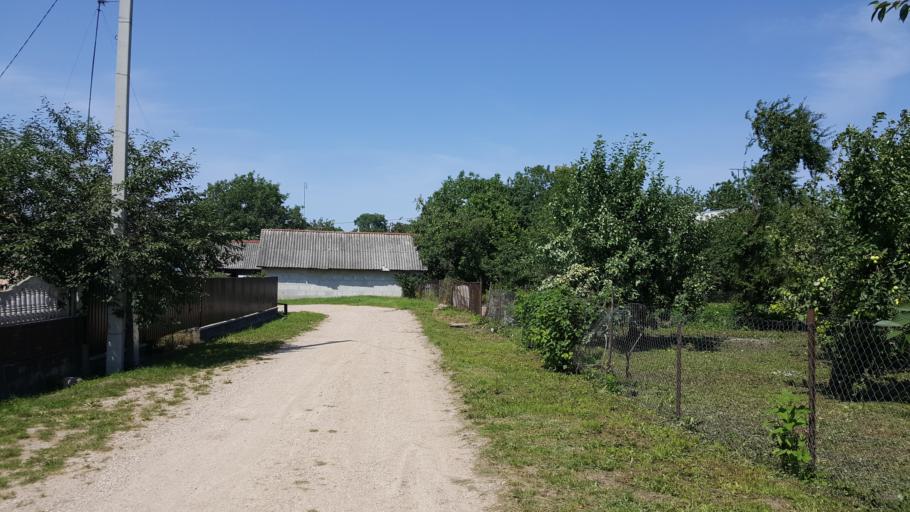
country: BY
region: Brest
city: Vysokaye
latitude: 52.3635
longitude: 23.3808
